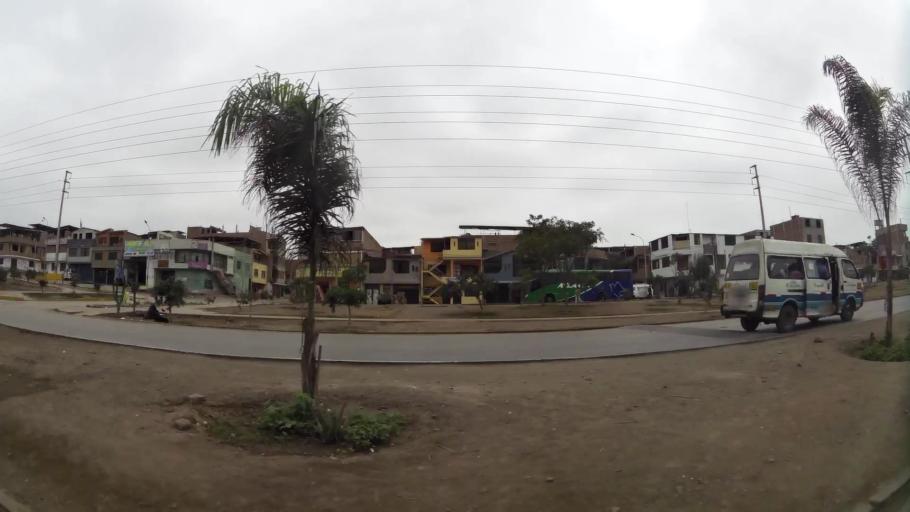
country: PE
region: Lima
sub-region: Lima
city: Surco
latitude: -12.1923
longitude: -76.9480
